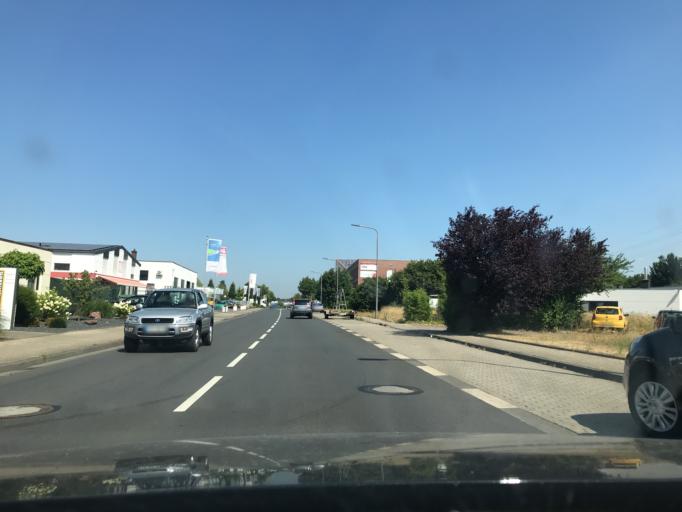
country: DE
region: North Rhine-Westphalia
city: Kempen
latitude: 51.3710
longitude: 6.4350
